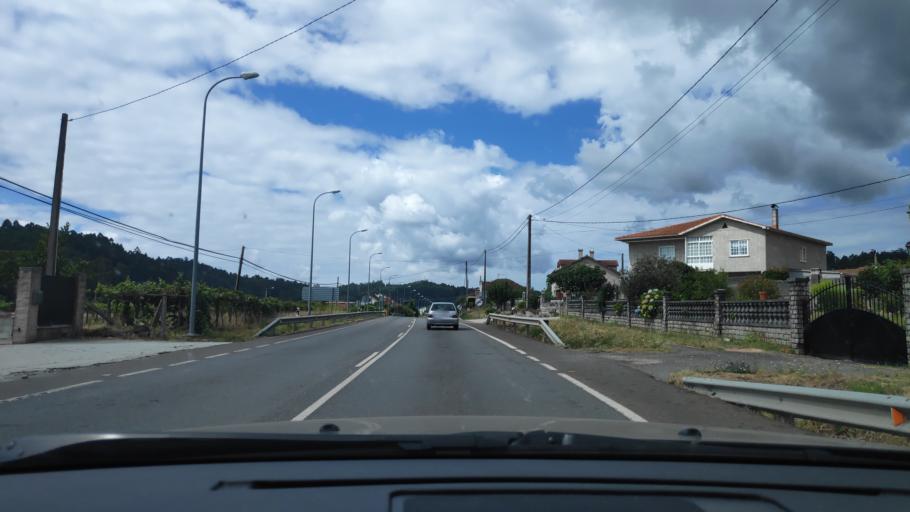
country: ES
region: Galicia
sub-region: Provincia de Pontevedra
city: Portas
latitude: 42.6014
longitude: -8.6580
